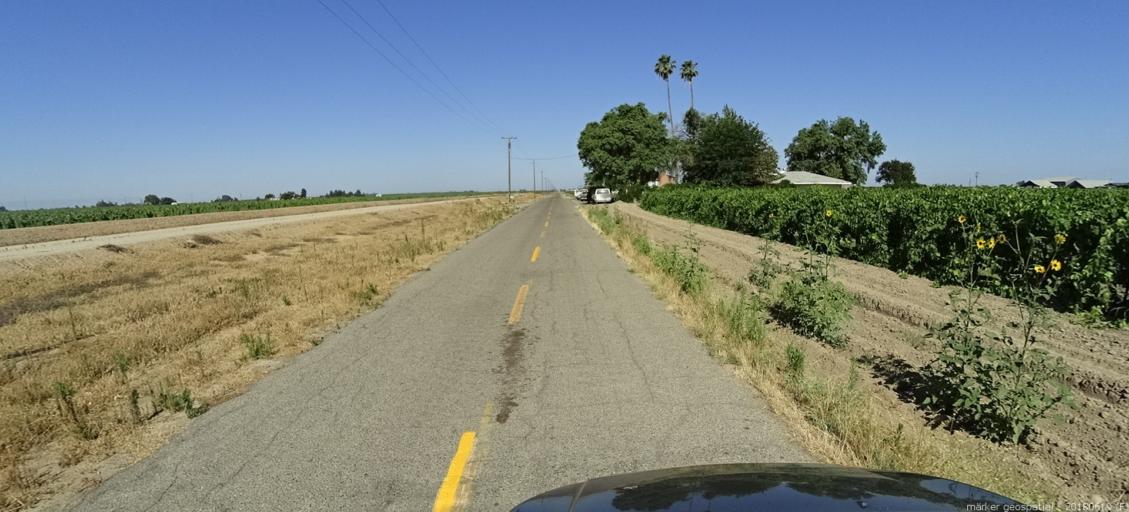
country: US
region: California
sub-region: Fresno County
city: Biola
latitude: 36.8368
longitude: -120.0082
